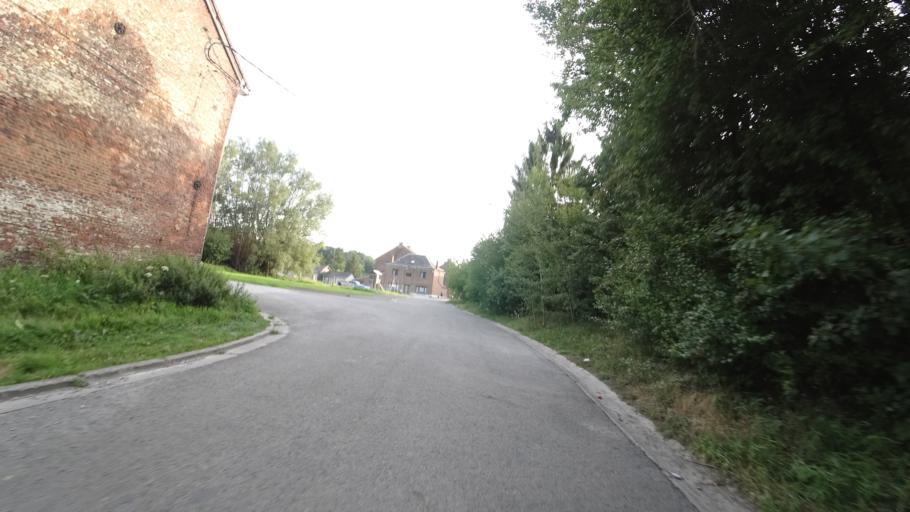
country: BE
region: Wallonia
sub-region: Province de Namur
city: Fosses-la-Ville
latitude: 50.4450
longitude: 4.6814
